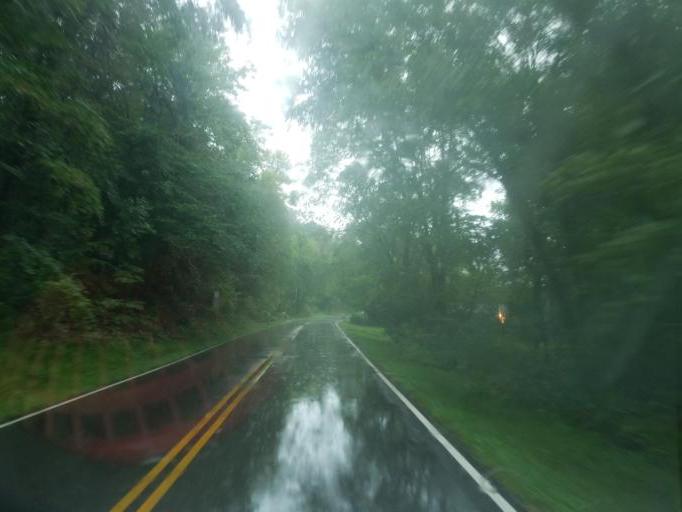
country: US
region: Kentucky
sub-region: Greenup County
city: Greenup
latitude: 38.5027
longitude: -82.9701
